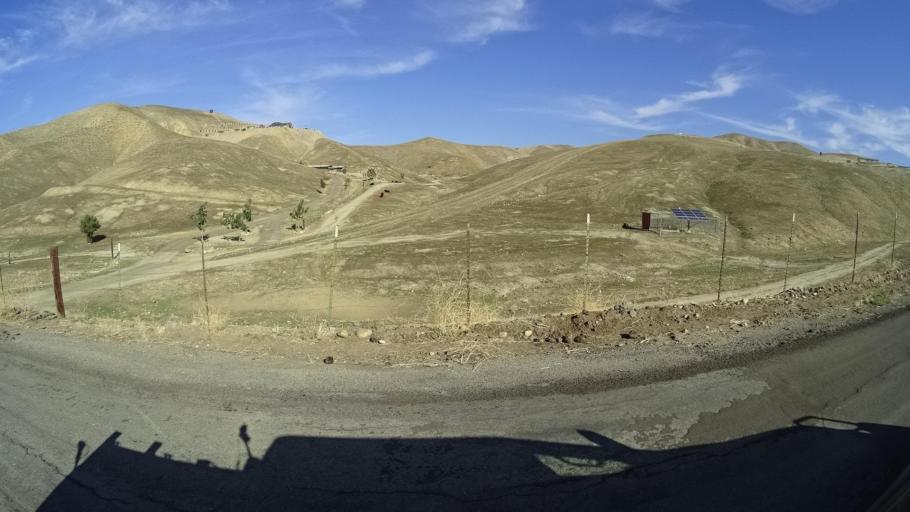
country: US
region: California
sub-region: Kern County
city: Lamont
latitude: 35.4027
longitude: -118.7943
